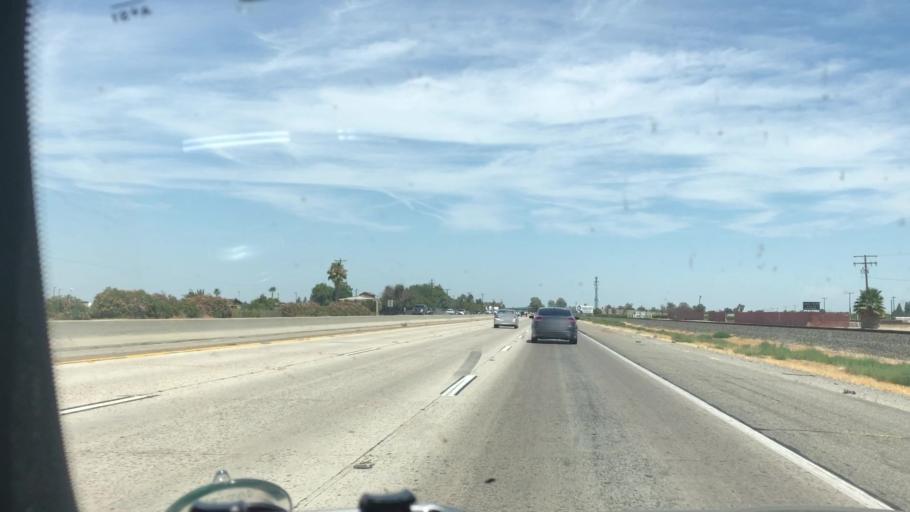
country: US
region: California
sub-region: Kern County
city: McFarland
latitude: 35.6639
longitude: -119.2237
